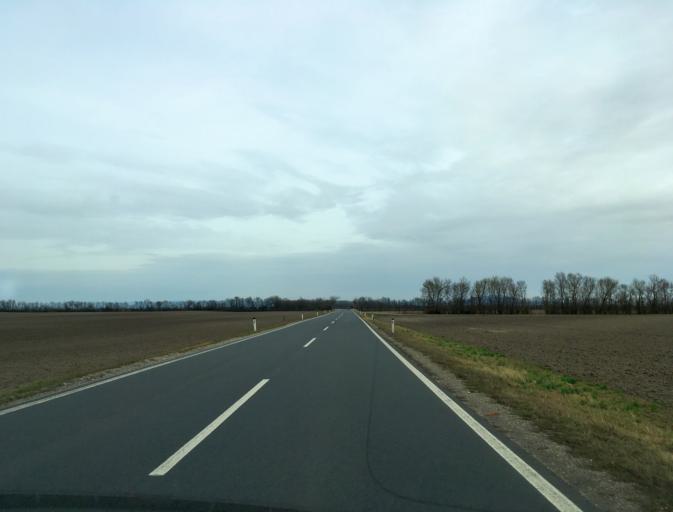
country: AT
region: Lower Austria
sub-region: Politischer Bezirk Ganserndorf
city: Untersiebenbrunn
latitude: 48.2227
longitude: 16.7617
